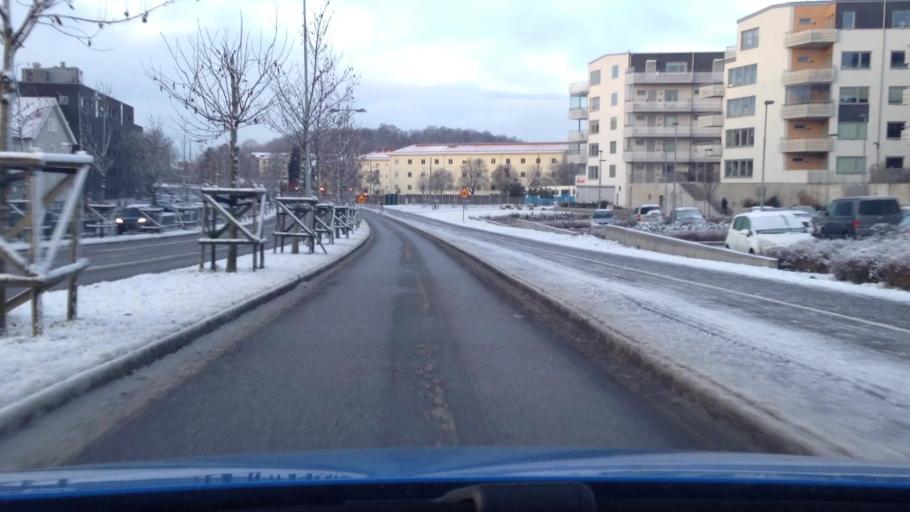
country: SE
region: Vaestra Goetaland
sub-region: Goteborg
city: Eriksbo
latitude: 57.7338
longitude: 12.0291
